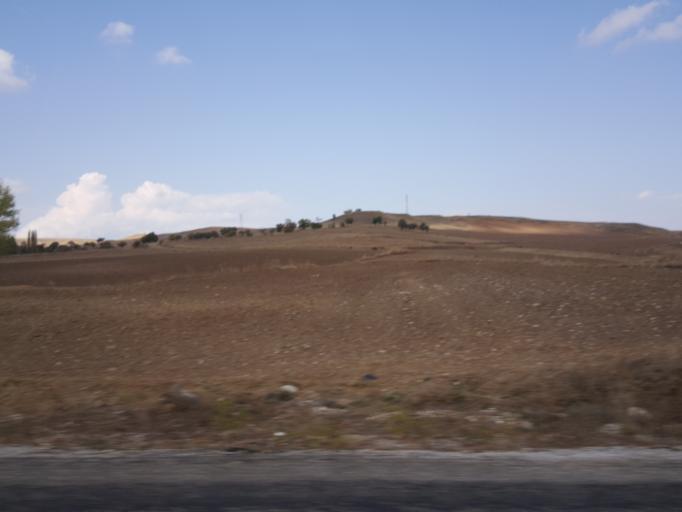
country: TR
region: Corum
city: Alaca
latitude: 40.1571
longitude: 34.7079
